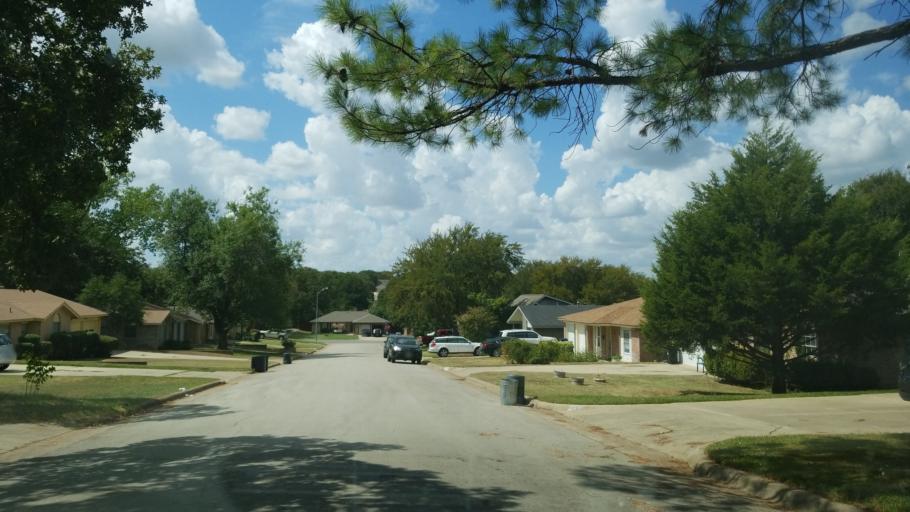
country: US
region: Texas
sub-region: Tarrant County
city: Euless
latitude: 32.8586
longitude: -97.0943
